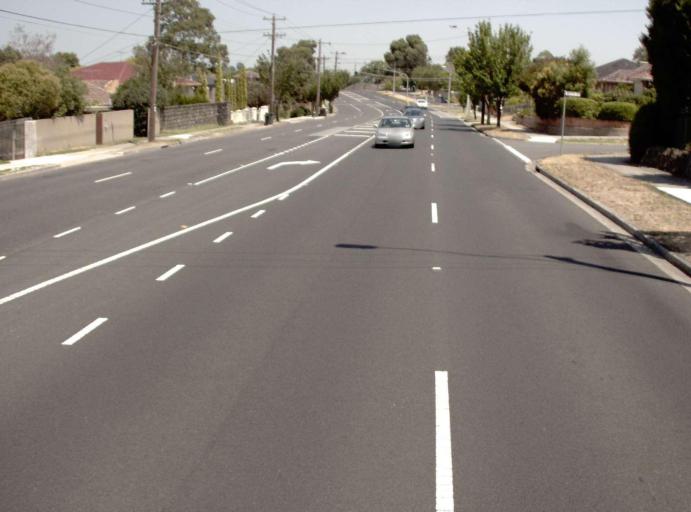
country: AU
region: Victoria
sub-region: Manningham
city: Bulleen
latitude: -37.7762
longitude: 145.0882
